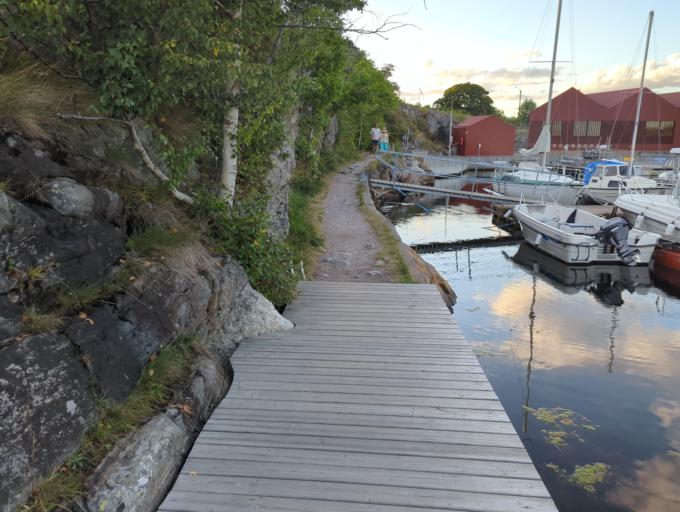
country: SE
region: Vaestra Goetaland
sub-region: Stromstads Kommun
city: Stroemstad
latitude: 58.8923
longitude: 11.0475
